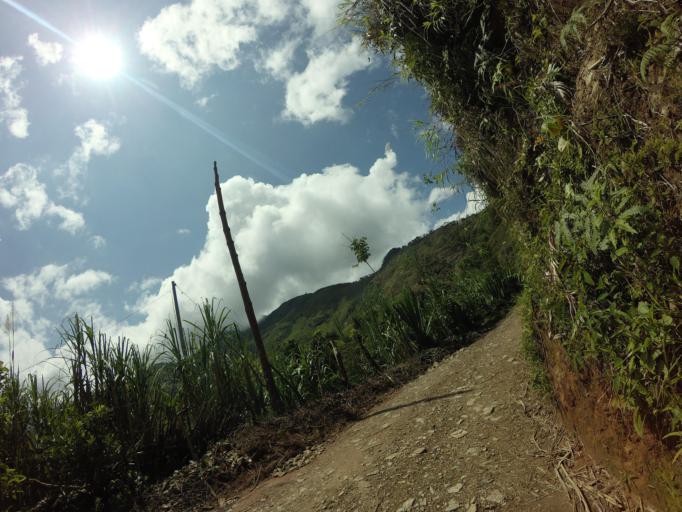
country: CO
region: Caldas
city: Pensilvania
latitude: 5.4797
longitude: -75.1840
